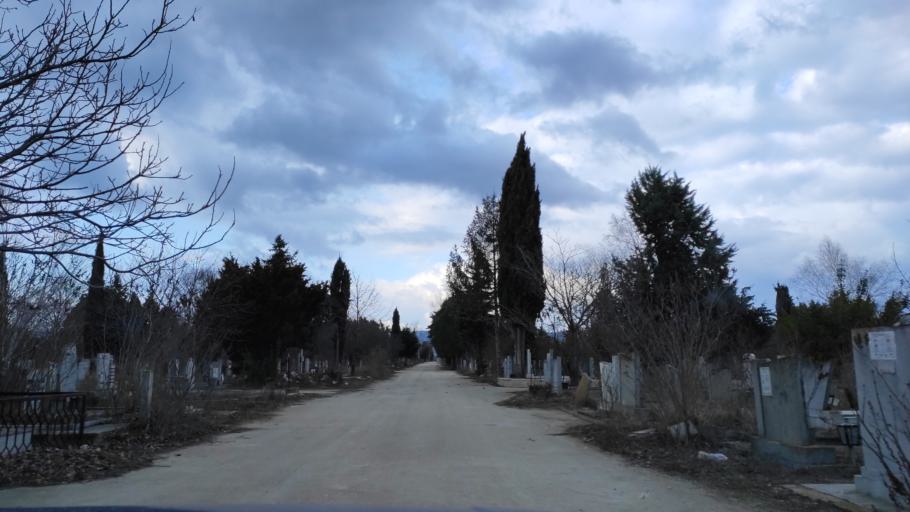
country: BG
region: Varna
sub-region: Obshtina Aksakovo
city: Aksakovo
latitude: 43.2181
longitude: 27.8089
